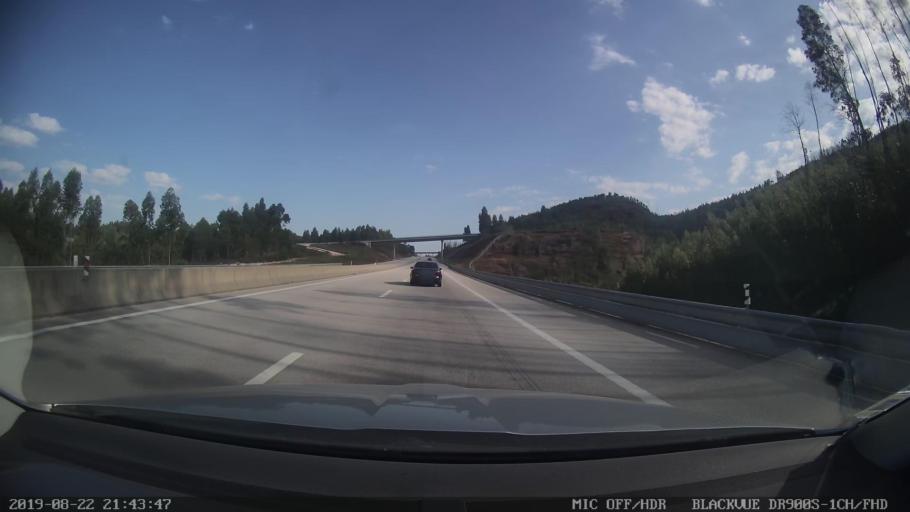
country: PT
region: Leiria
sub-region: Figueiro Dos Vinhos
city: Figueiro dos Vinhos
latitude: 39.9401
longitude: -8.3475
